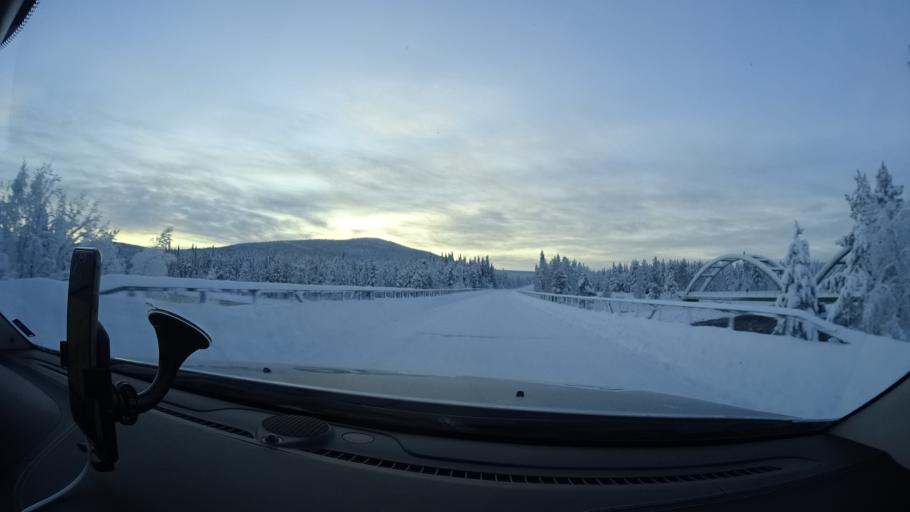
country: SE
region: Norrbotten
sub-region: Arvidsjaurs Kommun
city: Arvidsjaur
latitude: 65.9537
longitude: 19.5233
